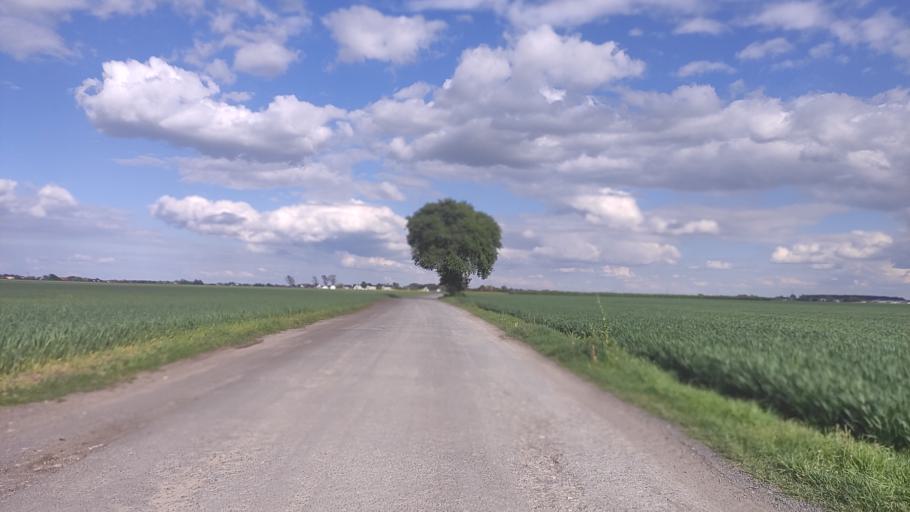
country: PL
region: Greater Poland Voivodeship
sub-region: Powiat poznanski
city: Swarzedz
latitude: 52.3878
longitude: 17.1299
